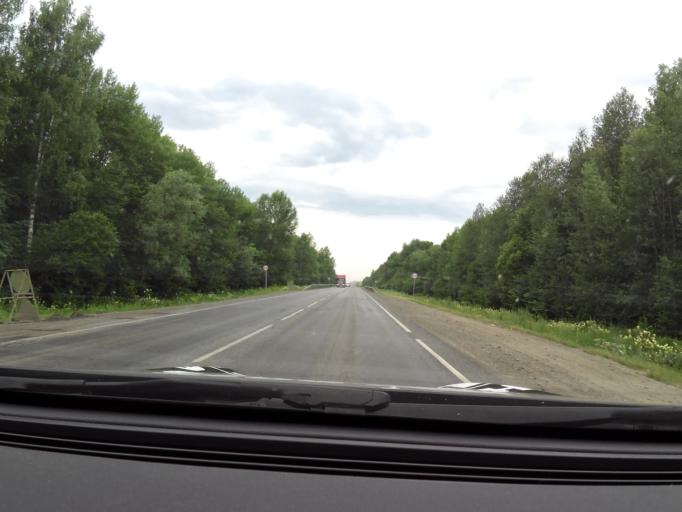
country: RU
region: Bashkortostan
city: Urman
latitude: 54.8174
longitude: 56.8410
